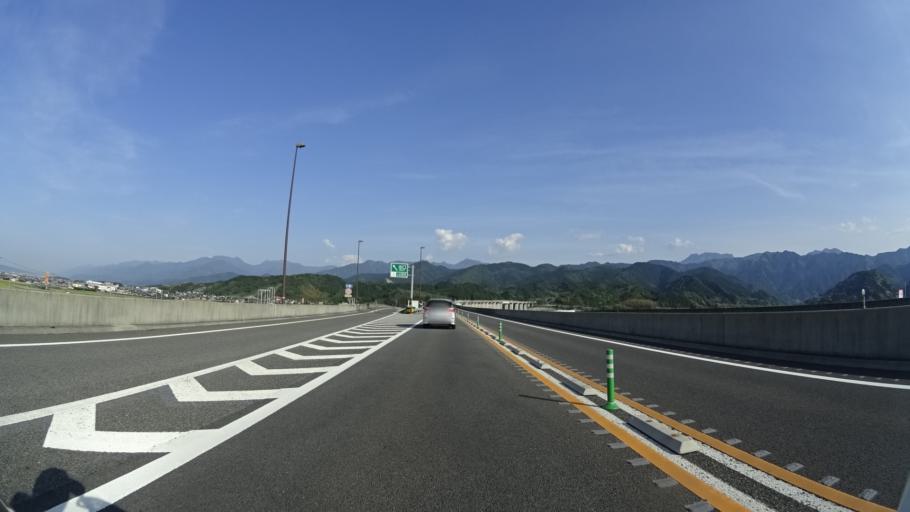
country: JP
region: Ehime
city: Saijo
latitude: 33.8953
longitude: 133.0804
